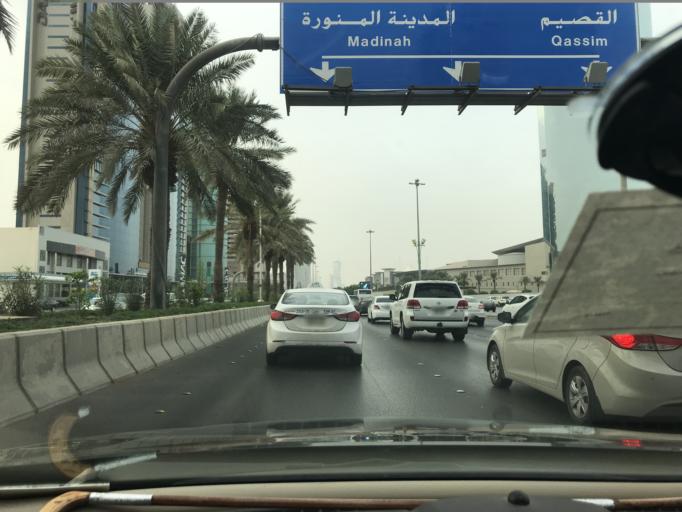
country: SA
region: Ar Riyad
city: Riyadh
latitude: 24.7078
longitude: 46.6743
